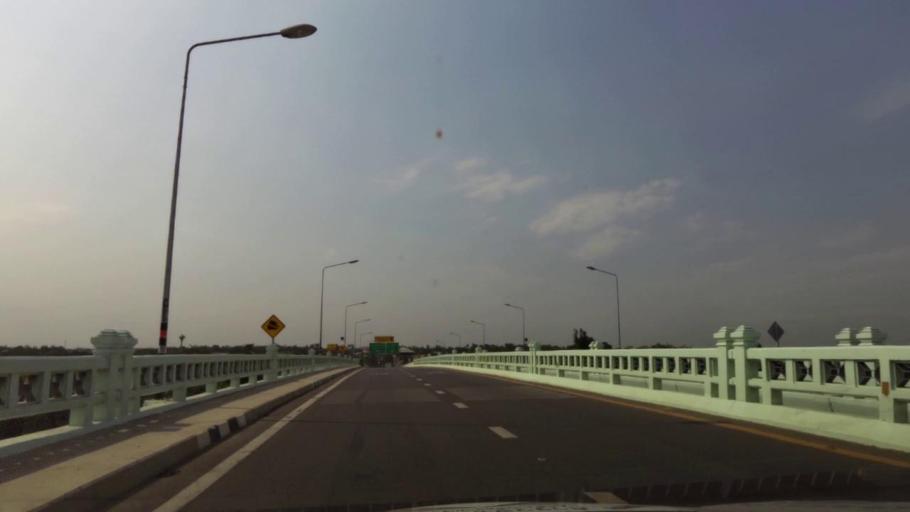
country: TH
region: Phra Nakhon Si Ayutthaya
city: Phra Nakhon Si Ayutthaya
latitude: 14.3310
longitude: 100.5752
